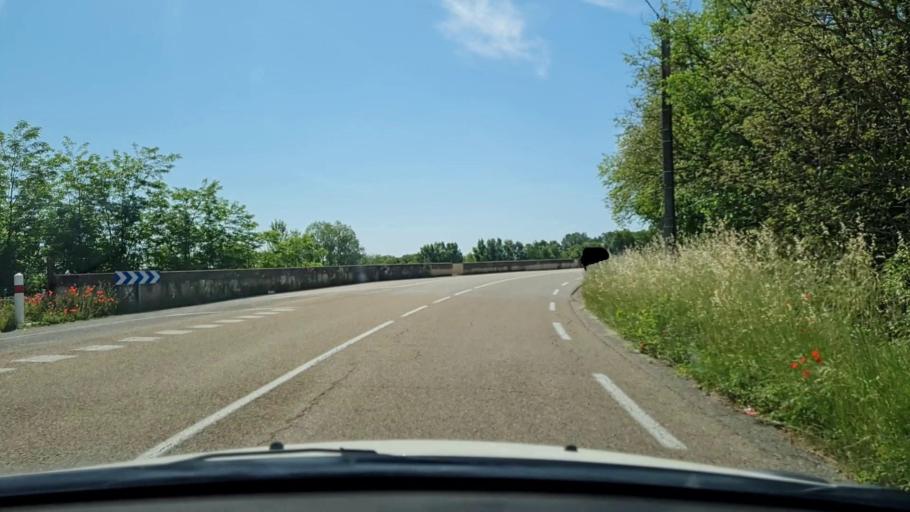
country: FR
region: Languedoc-Roussillon
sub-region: Departement du Gard
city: Vezenobres
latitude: 44.0190
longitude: 4.1556
